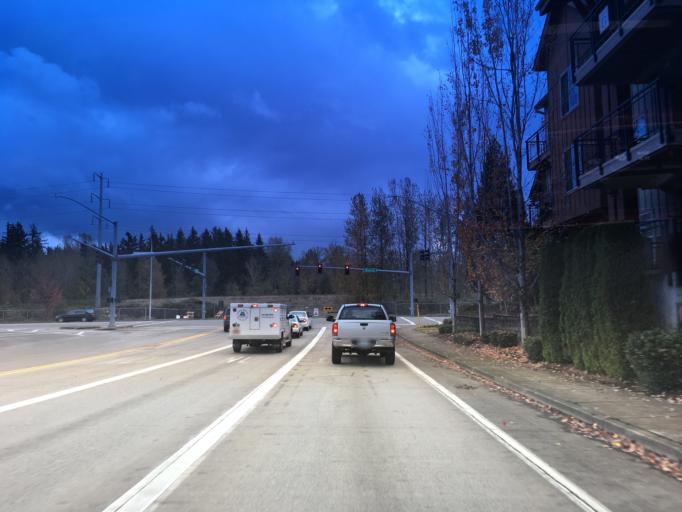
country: US
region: Oregon
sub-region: Multnomah County
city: Fairview
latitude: 45.5284
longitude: -122.4426
